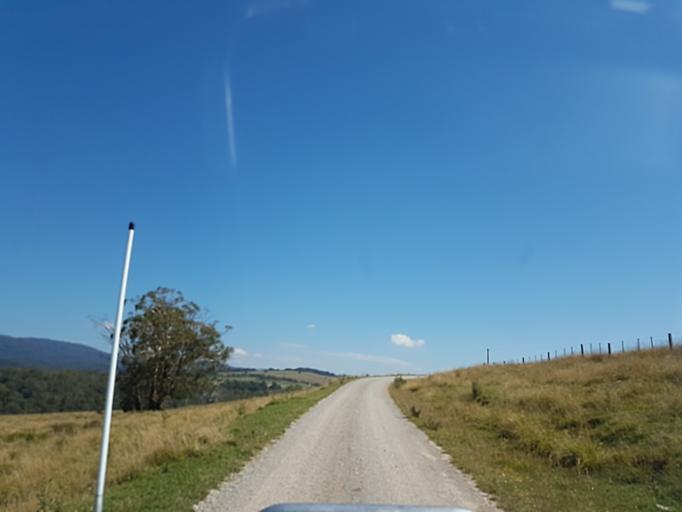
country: AU
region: Victoria
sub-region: East Gippsland
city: Lakes Entrance
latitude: -37.2330
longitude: 148.2692
